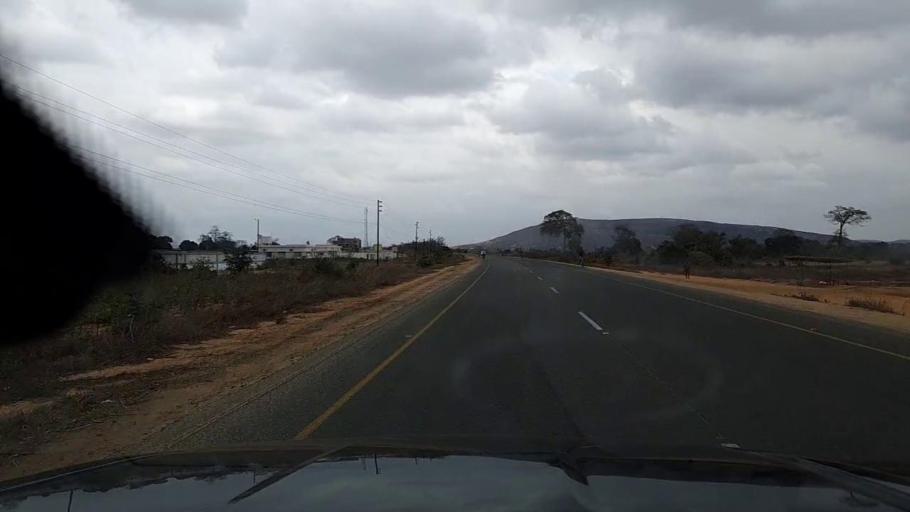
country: MZ
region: Nampula
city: Nampula
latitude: -15.1613
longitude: 39.3066
